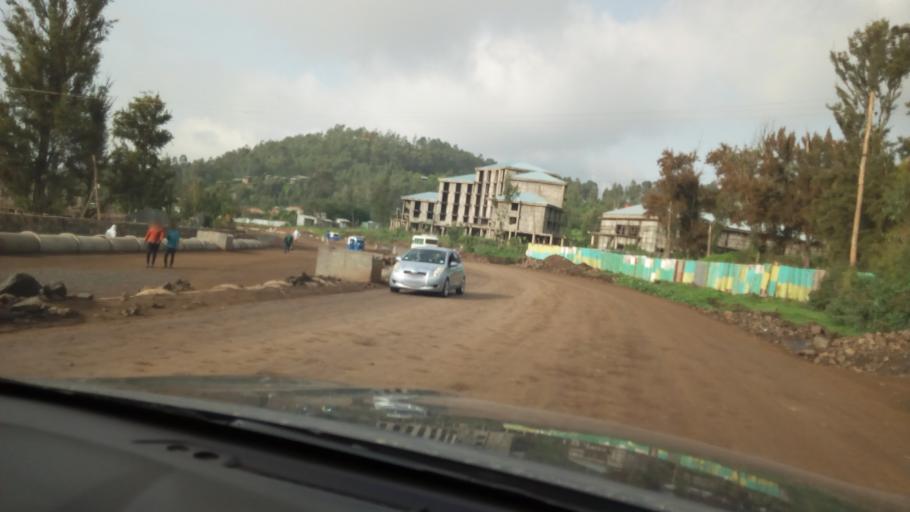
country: ET
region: Amhara
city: Gondar
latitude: 12.5736
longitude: 37.4322
